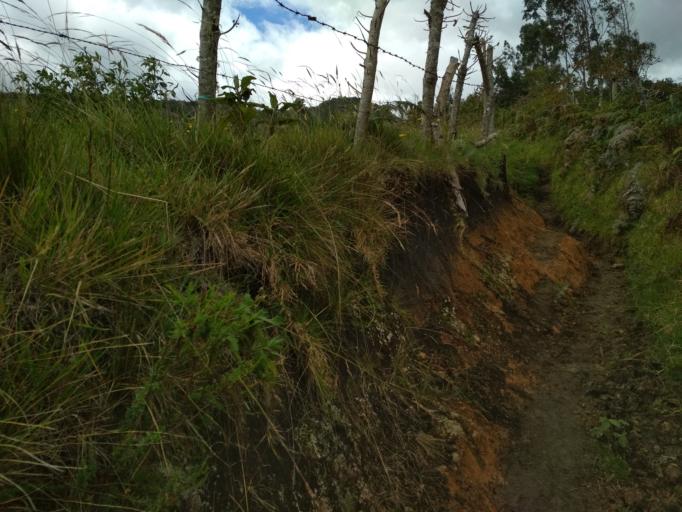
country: CO
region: Cauca
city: Totoro
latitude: 2.5194
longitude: -76.3903
